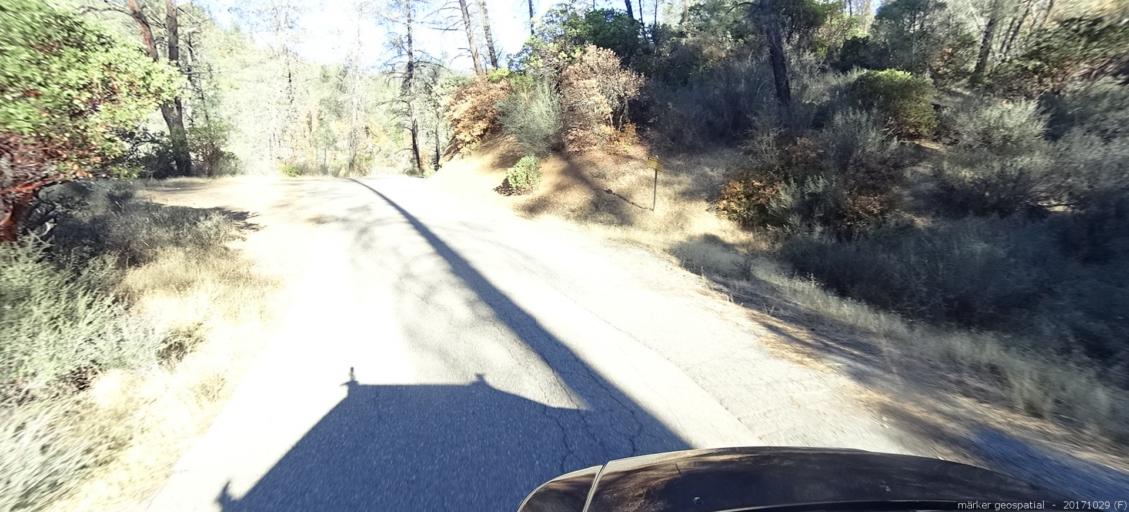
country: US
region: California
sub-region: Trinity County
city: Hayfork
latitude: 40.3727
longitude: -122.9755
